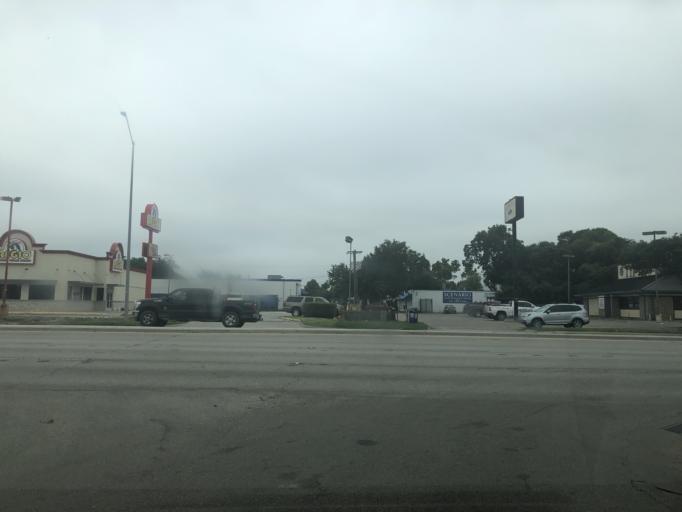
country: US
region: Texas
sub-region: Dallas County
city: University Park
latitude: 32.8554
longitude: -96.8672
